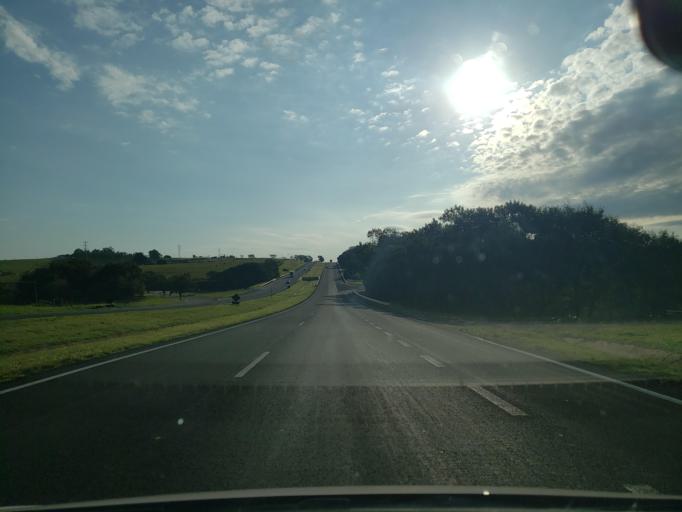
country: BR
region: Sao Paulo
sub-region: Valparaiso
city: Valparaiso
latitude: -21.2101
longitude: -50.8723
